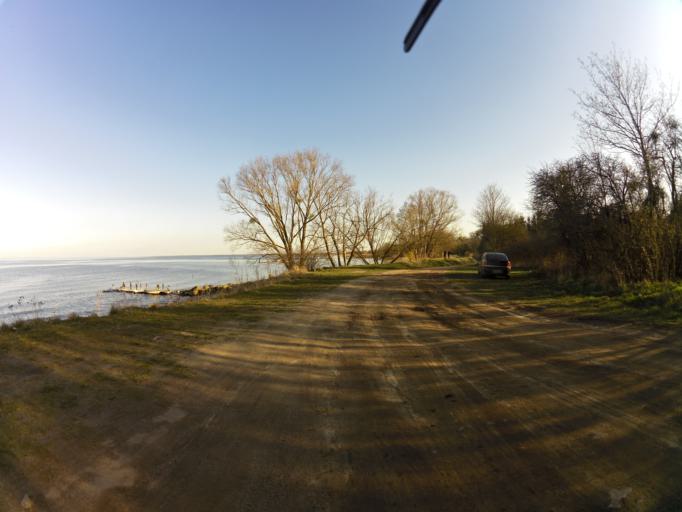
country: PL
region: West Pomeranian Voivodeship
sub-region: Powiat policki
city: Nowe Warpno
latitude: 53.7327
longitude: 14.3321
